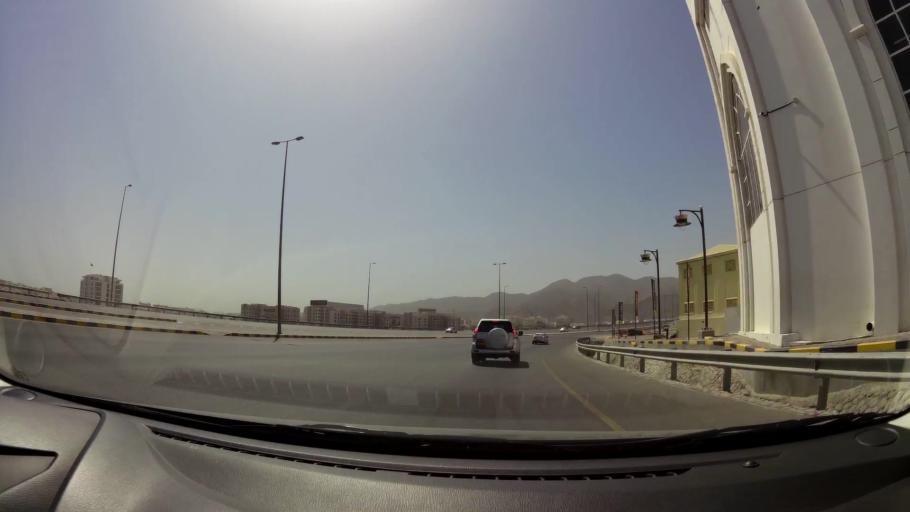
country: OM
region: Muhafazat Masqat
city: Bawshar
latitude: 23.5871
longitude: 58.4144
